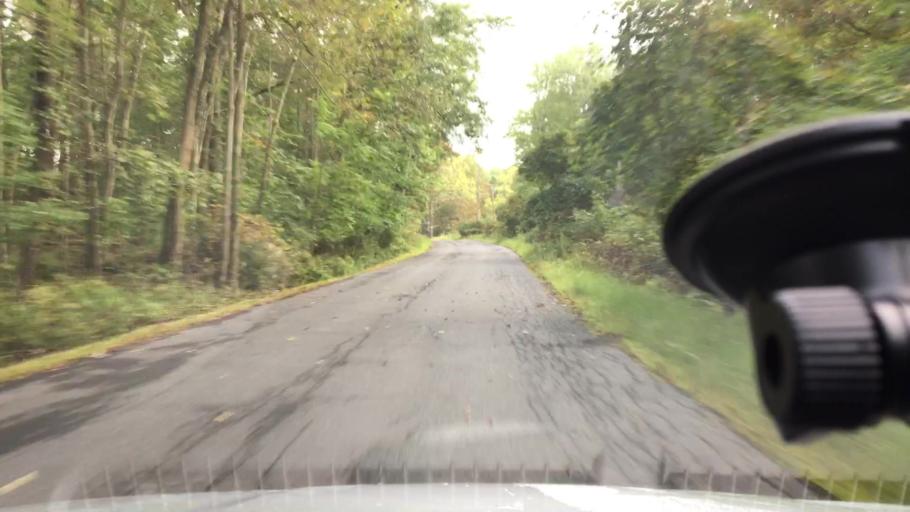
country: US
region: Pennsylvania
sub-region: Monroe County
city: Mountainhome
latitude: 41.1492
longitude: -75.2552
